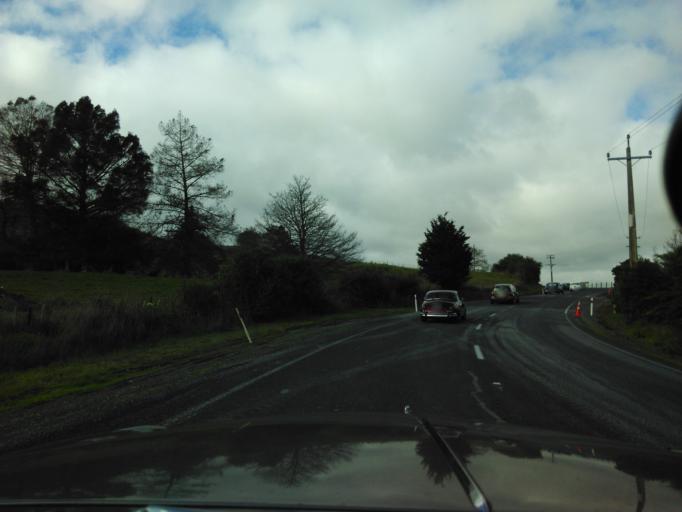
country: NZ
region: Auckland
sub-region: Auckland
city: Pukekohe East
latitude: -37.1479
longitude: 174.9953
